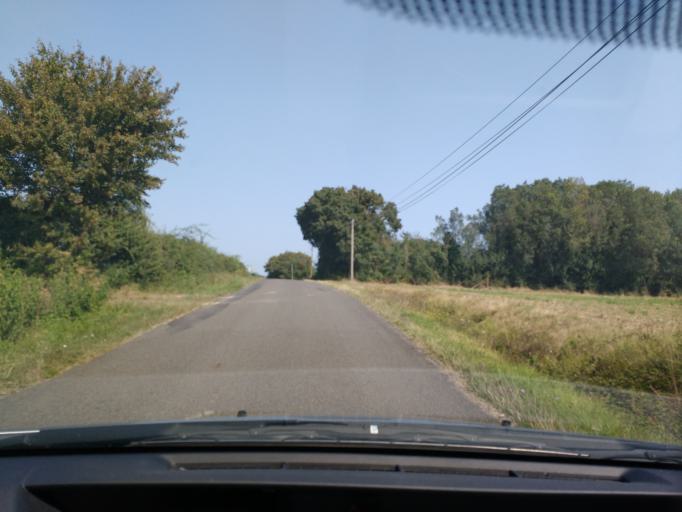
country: FR
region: Pays de la Loire
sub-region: Departement de Maine-et-Loire
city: Bauge-en-Anjou
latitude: 47.5437
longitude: -0.0380
